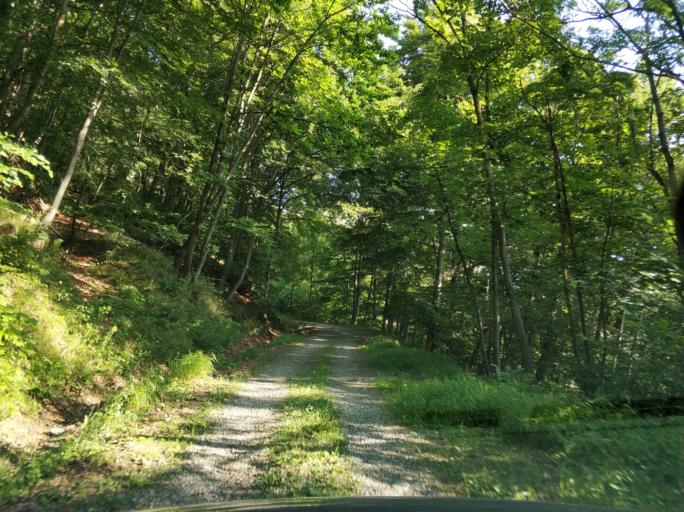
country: IT
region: Piedmont
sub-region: Provincia di Torino
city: Ceres
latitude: 45.3086
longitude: 7.3654
